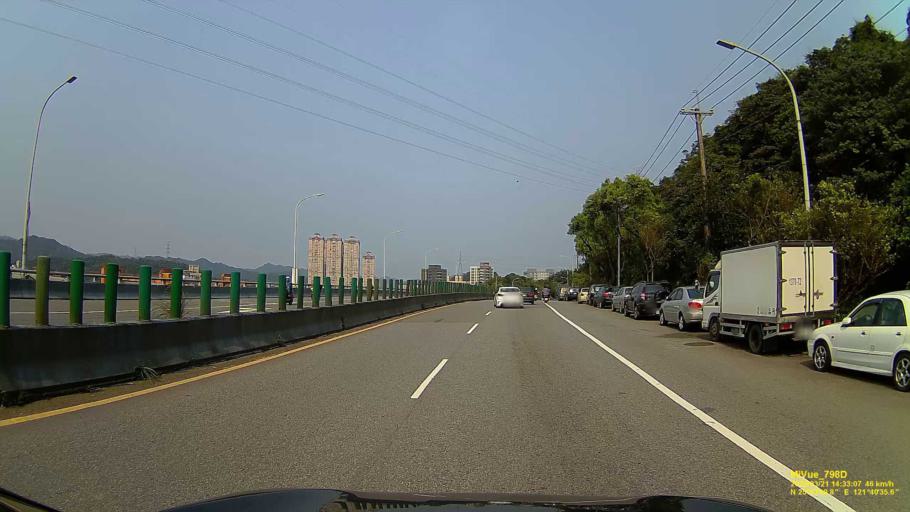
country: TW
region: Taiwan
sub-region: Keelung
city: Keelung
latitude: 25.0667
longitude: 121.6767
